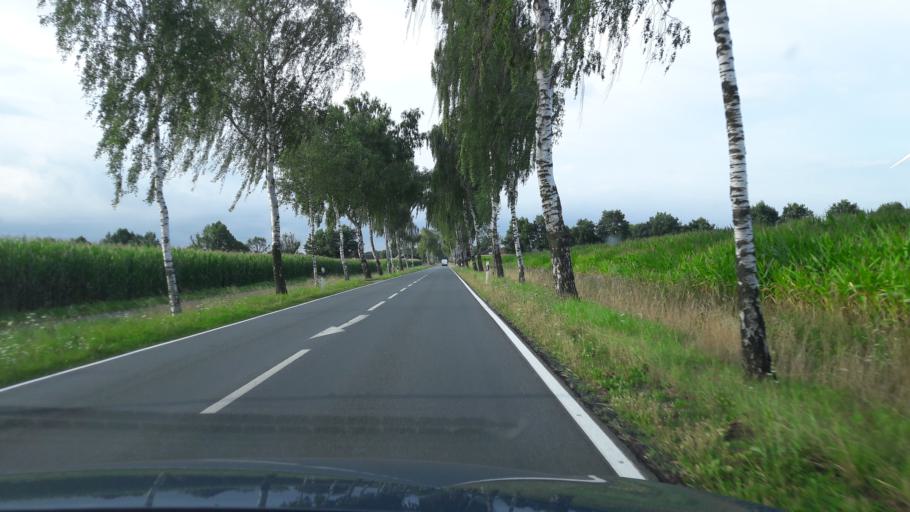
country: DE
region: North Rhine-Westphalia
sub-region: Regierungsbezirk Munster
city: Everswinkel
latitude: 51.8911
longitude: 7.8896
